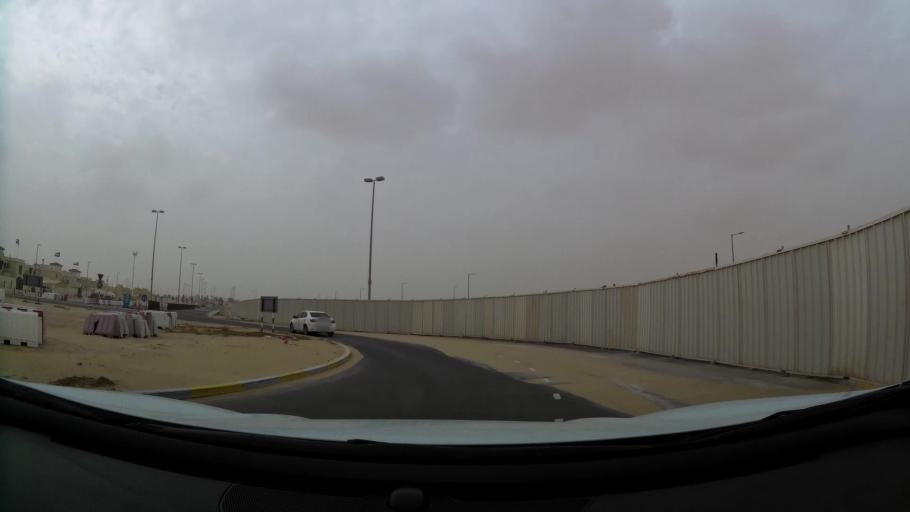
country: AE
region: Abu Dhabi
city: Abu Dhabi
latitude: 24.4328
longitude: 54.7265
